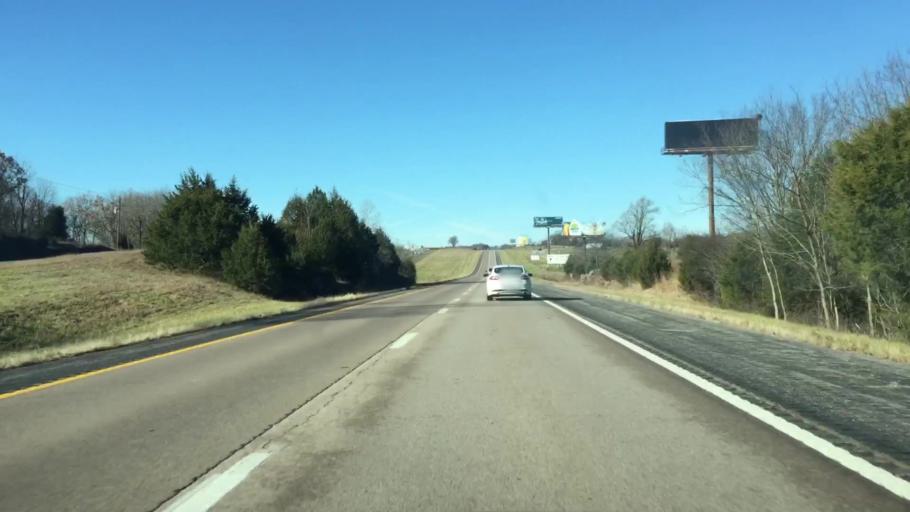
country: US
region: Missouri
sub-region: Miller County
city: Eldon
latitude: 38.3678
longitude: -92.4955
